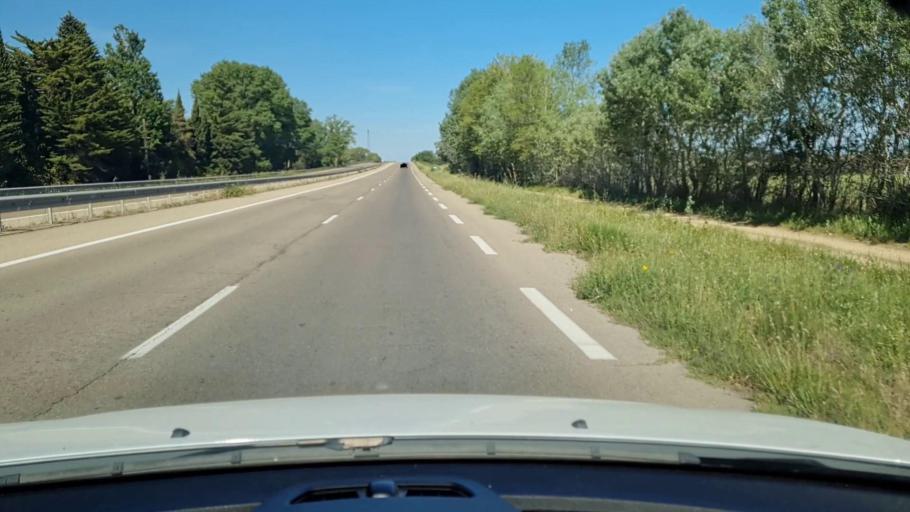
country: FR
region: Languedoc-Roussillon
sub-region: Departement du Gard
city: Le Grau-du-Roi
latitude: 43.5609
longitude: 4.1488
